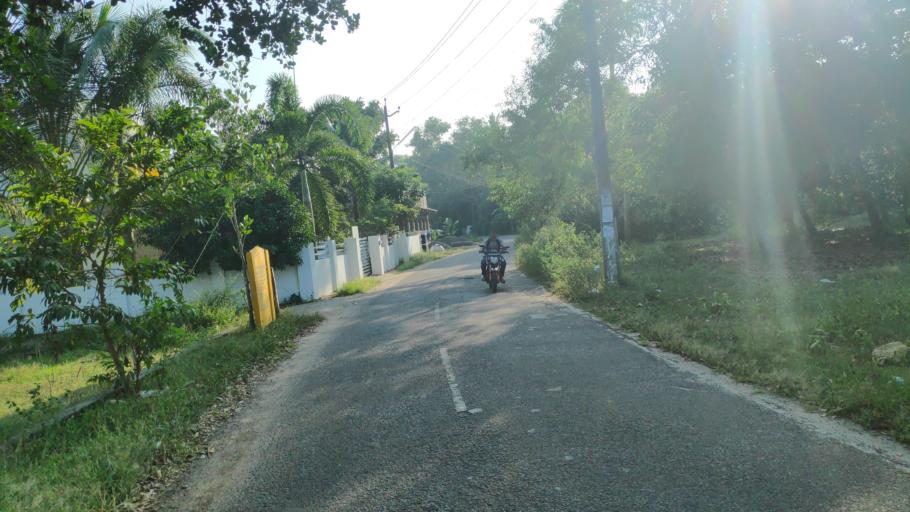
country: IN
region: Kerala
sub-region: Alappuzha
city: Alleppey
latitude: 9.5827
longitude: 76.3414
